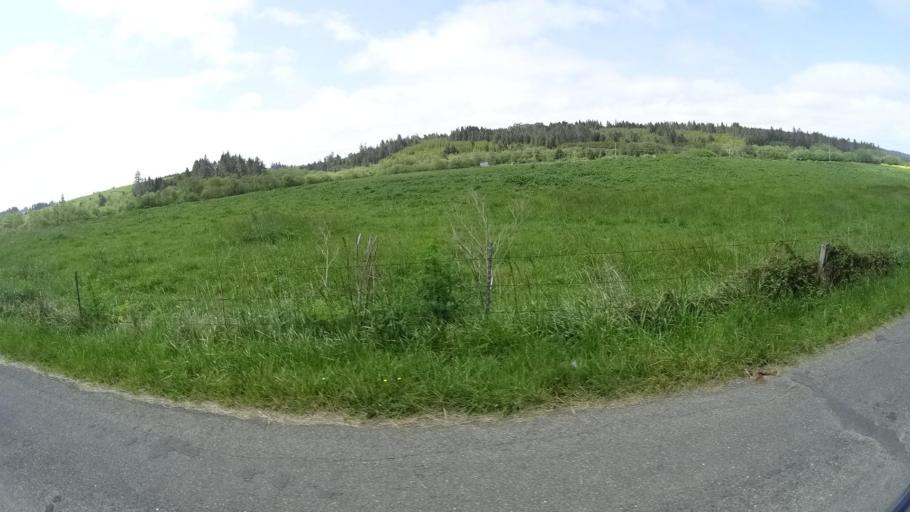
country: US
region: California
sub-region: Humboldt County
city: Humboldt Hill
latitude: 40.6626
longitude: -124.1923
